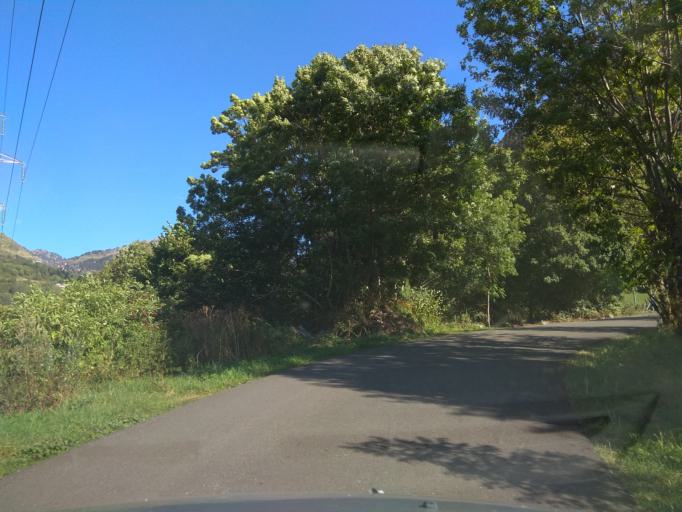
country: ES
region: Catalonia
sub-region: Provincia de Lleida
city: Vielha
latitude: 42.7014
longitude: 0.9111
